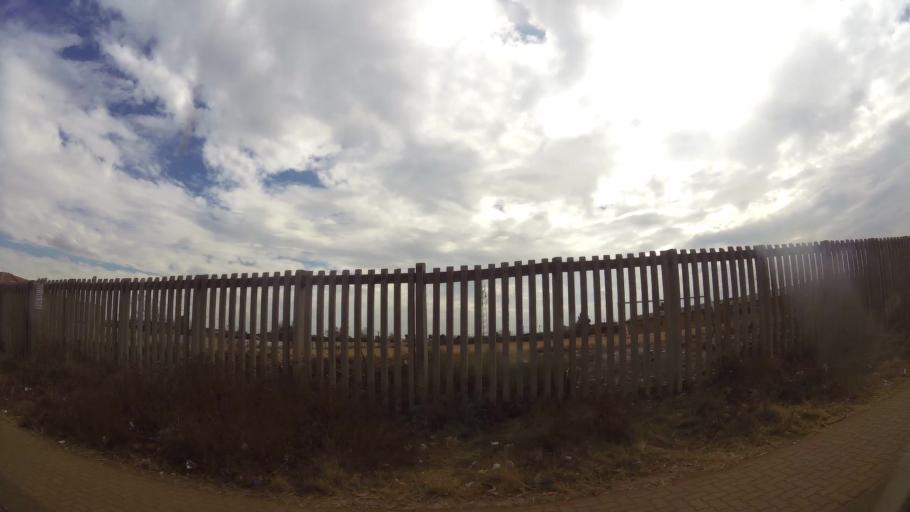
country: ZA
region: Gauteng
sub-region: Ekurhuleni Metropolitan Municipality
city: Germiston
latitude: -26.4011
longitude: 28.1480
